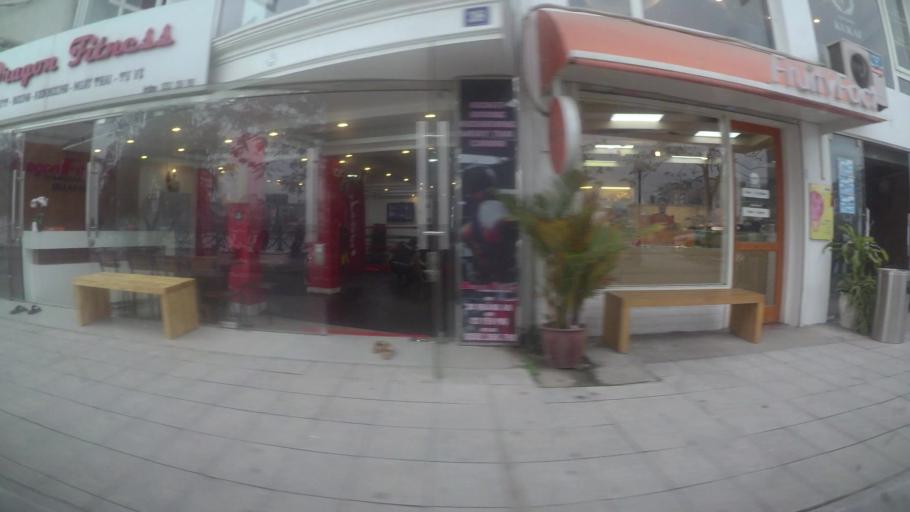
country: VN
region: Ha Noi
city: Tay Ho
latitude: 21.0615
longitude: 105.8284
